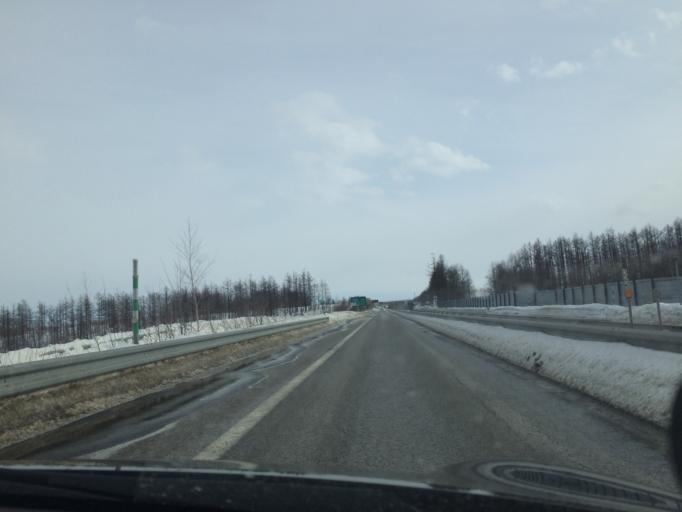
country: JP
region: Hokkaido
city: Otofuke
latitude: 43.0014
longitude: 142.8487
